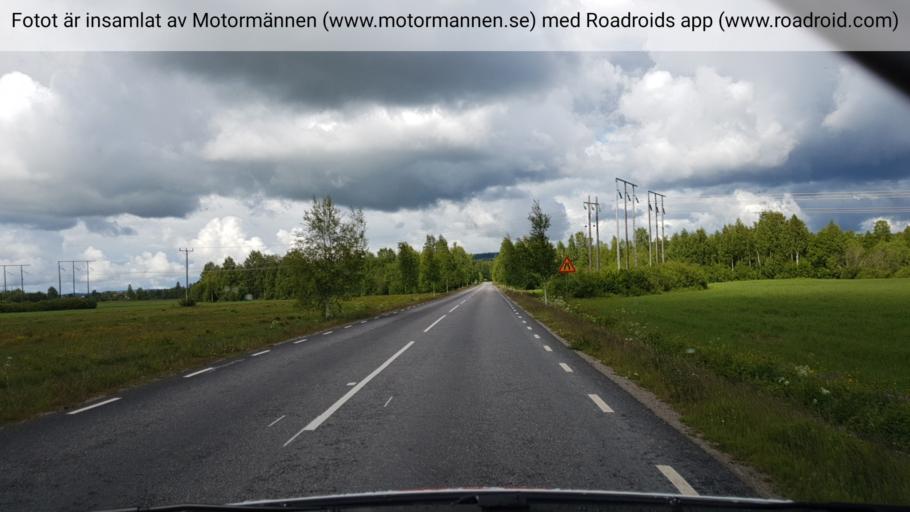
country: SE
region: Vaesterbotten
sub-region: Vannas Kommun
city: Vannasby
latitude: 63.8848
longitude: 19.8880
